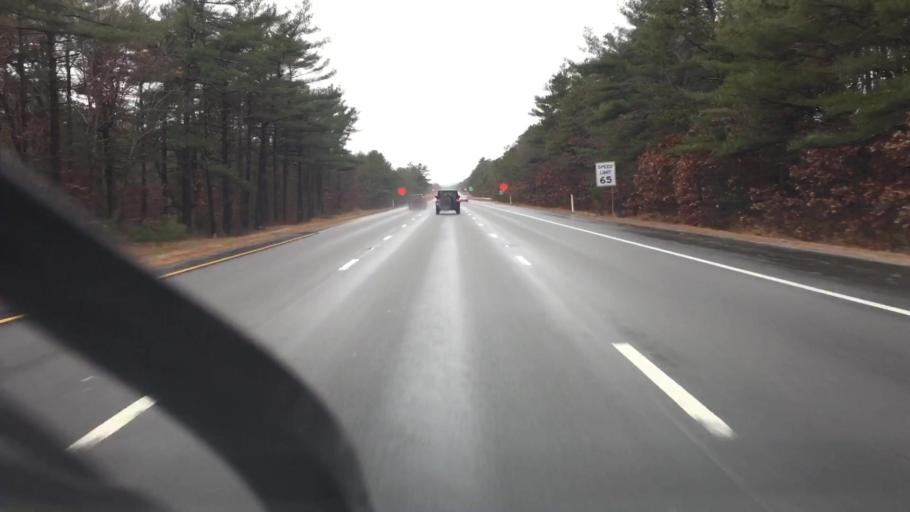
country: US
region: Massachusetts
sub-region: Plymouth County
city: Wareham Center
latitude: 41.7701
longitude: -70.6874
